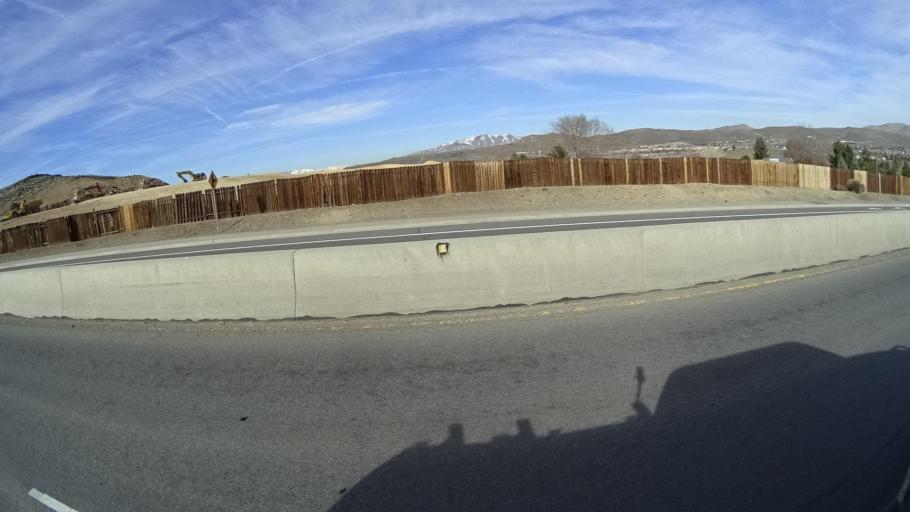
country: US
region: Nevada
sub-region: Washoe County
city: Sparks
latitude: 39.5726
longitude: -119.7204
